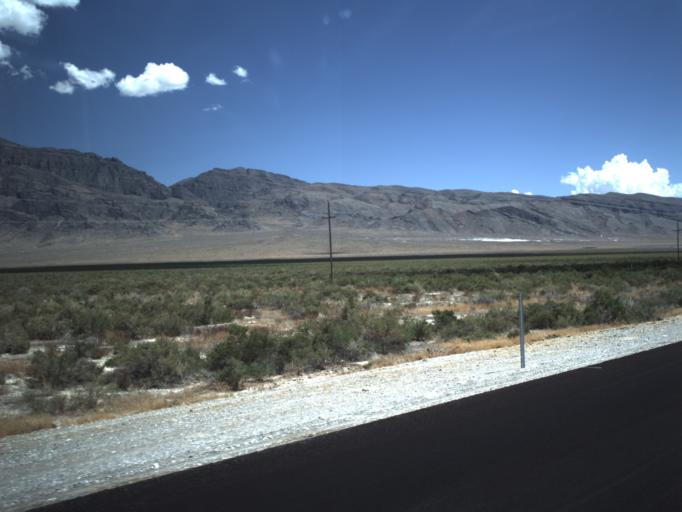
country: US
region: Utah
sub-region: Beaver County
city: Milford
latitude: 39.0806
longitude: -113.4884
